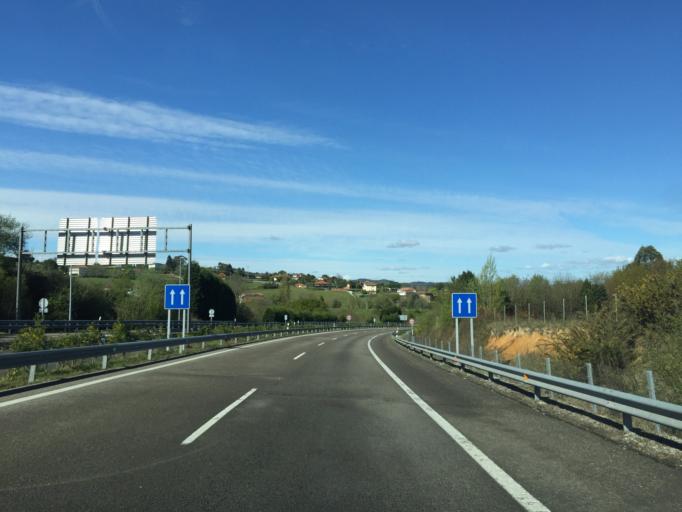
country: ES
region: Asturias
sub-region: Province of Asturias
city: Oviedo
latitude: 43.3477
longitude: -5.9008
